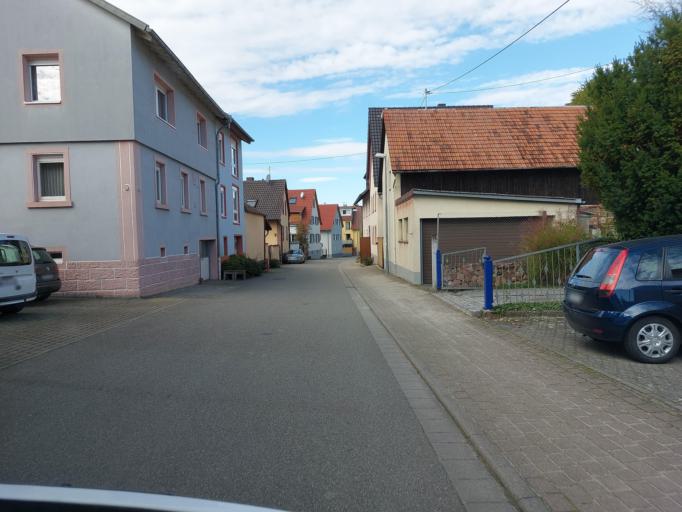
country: DE
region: Baden-Wuerttemberg
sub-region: Freiburg Region
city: Malterdingen
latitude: 48.1610
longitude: 7.7990
